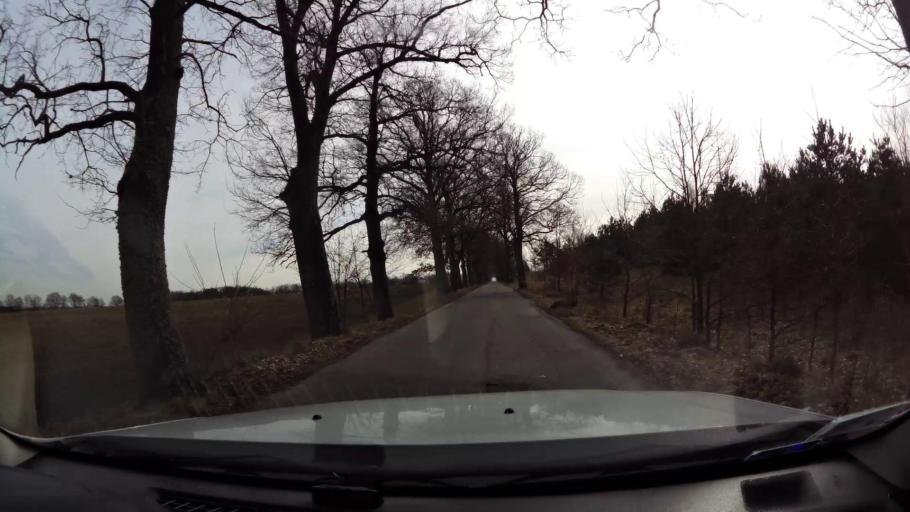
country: PL
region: West Pomeranian Voivodeship
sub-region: Powiat stargardzki
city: Insko
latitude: 53.4501
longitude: 15.6384
